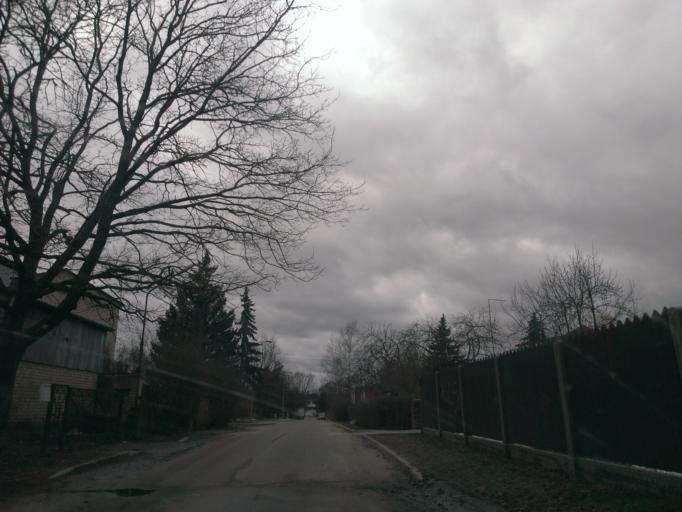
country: LV
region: Salaspils
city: Salaspils
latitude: 56.8589
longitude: 24.3545
